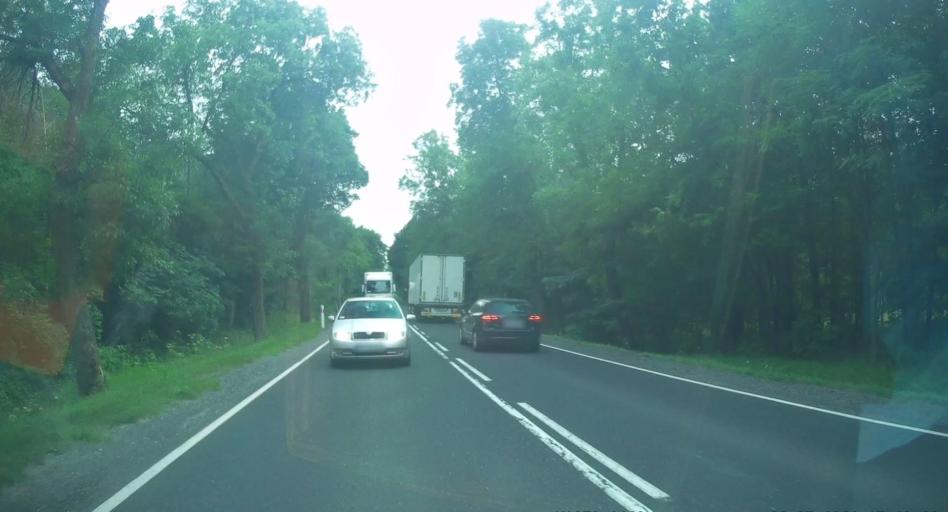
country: PL
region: Lodz Voivodeship
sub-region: Powiat radomszczanski
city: Gomunice
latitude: 51.1477
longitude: 19.4880
